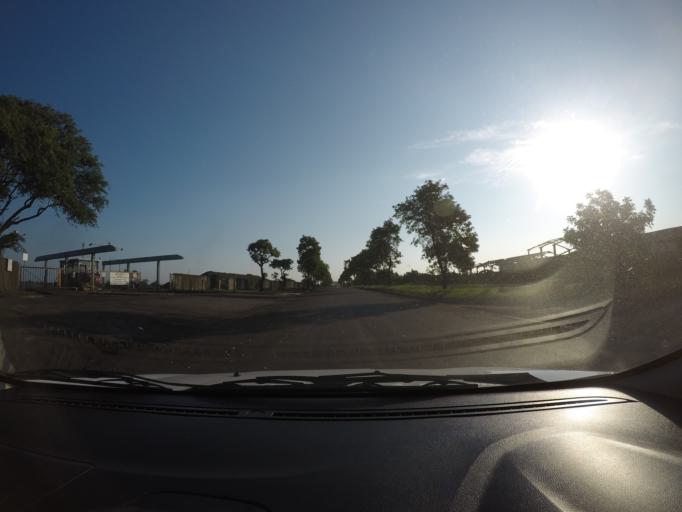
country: ZA
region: KwaZulu-Natal
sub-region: uThungulu District Municipality
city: Richards Bay
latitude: -28.7589
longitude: 32.0093
